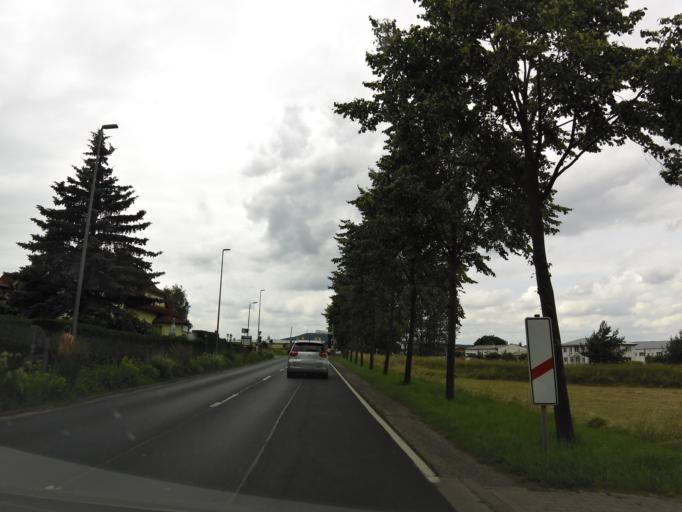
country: DE
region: Thuringia
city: Leimbach
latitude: 50.8163
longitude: 10.1916
